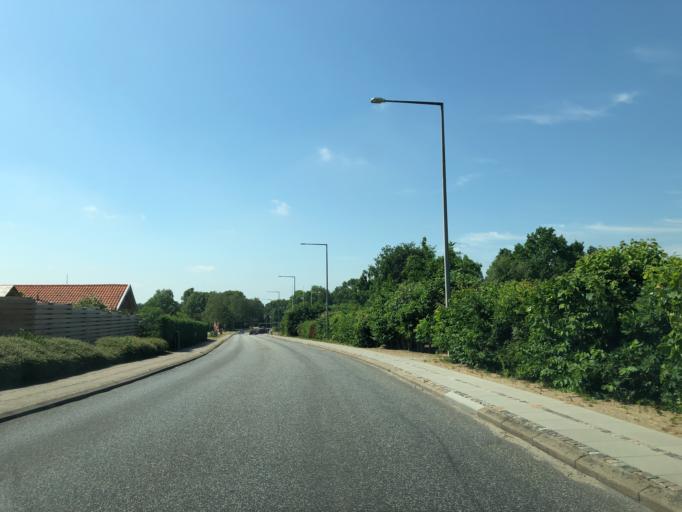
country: DK
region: South Denmark
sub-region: Kolding Kommune
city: Kolding
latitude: 55.5200
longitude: 9.4795
